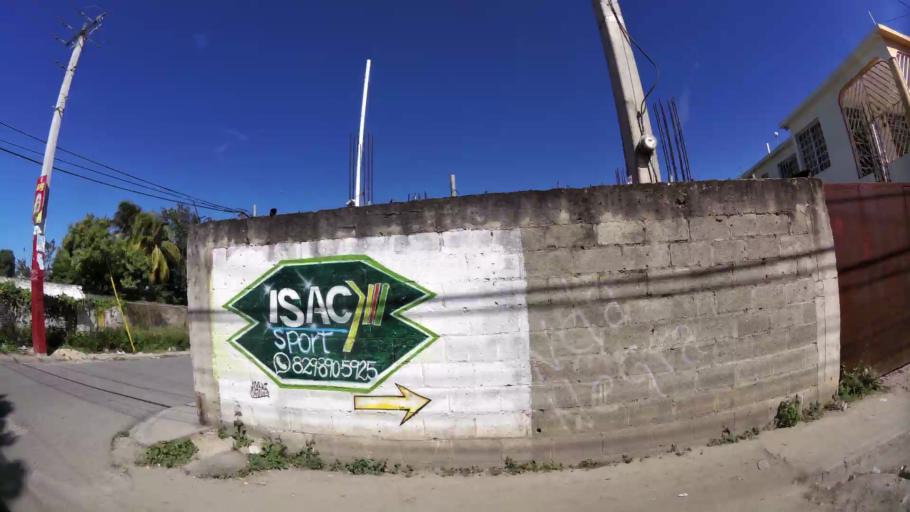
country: DO
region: San Cristobal
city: San Cristobal
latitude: 18.4305
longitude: -70.1185
